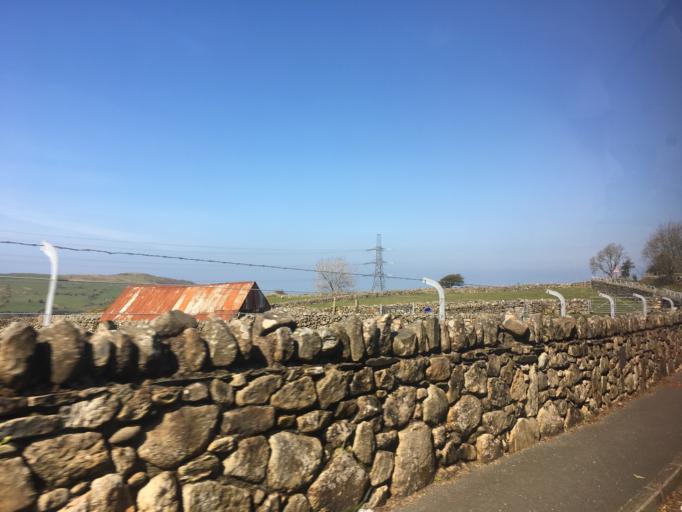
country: GB
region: Wales
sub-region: Gwynedd
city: Llanwnda
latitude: 53.0274
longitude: -4.2817
